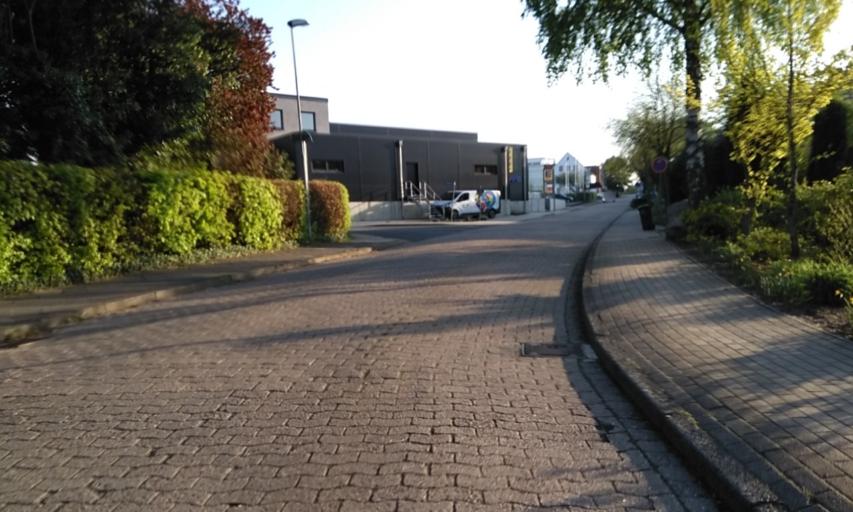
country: DE
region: Lower Saxony
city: Dollern
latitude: 53.5427
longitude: 9.5569
